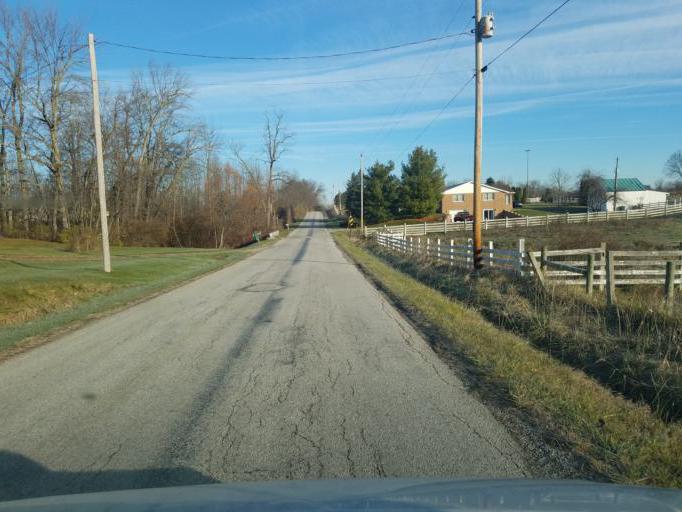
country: US
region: Ohio
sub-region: Morrow County
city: Mount Gilead
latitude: 40.6392
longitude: -82.9180
